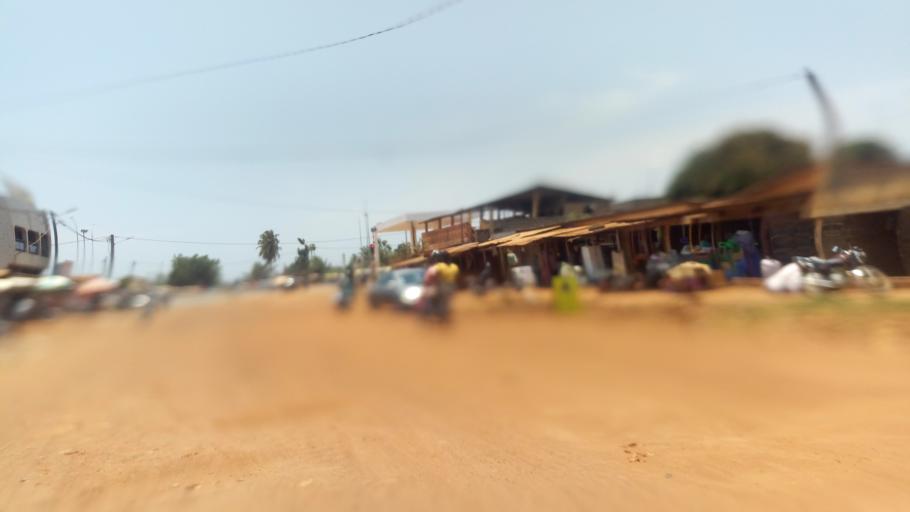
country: TG
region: Maritime
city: Lome
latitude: 6.2309
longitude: 1.1946
